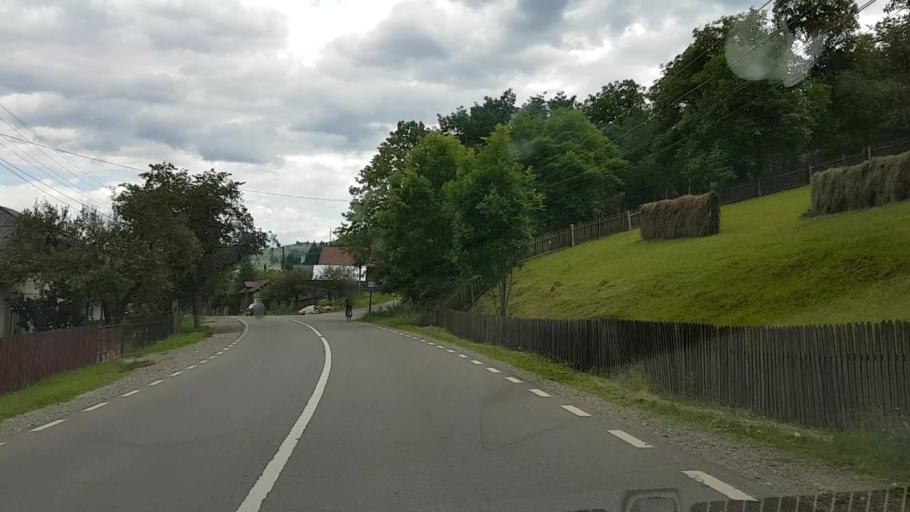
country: RO
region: Neamt
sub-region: Comuna Borca
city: Borca
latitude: 47.1851
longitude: 25.7746
